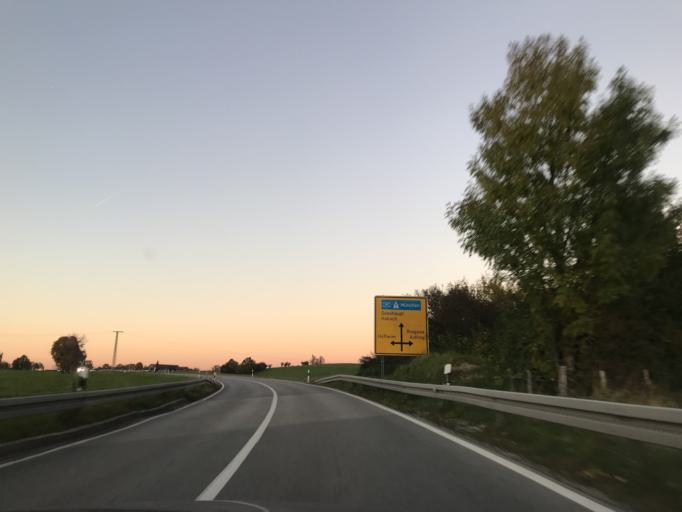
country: DE
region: Bavaria
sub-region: Upper Bavaria
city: Obersochering
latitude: 47.7151
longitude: 11.2227
